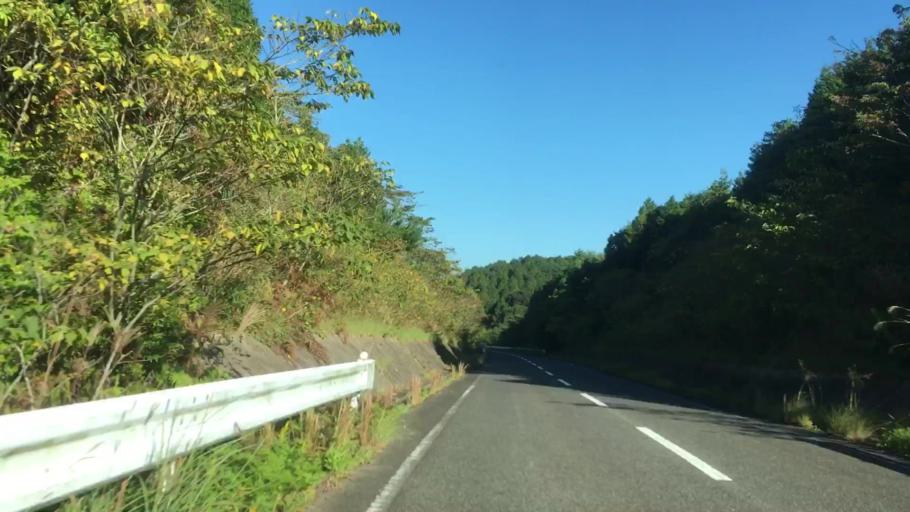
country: JP
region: Nagasaki
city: Sasebo
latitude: 33.0224
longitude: 129.6986
